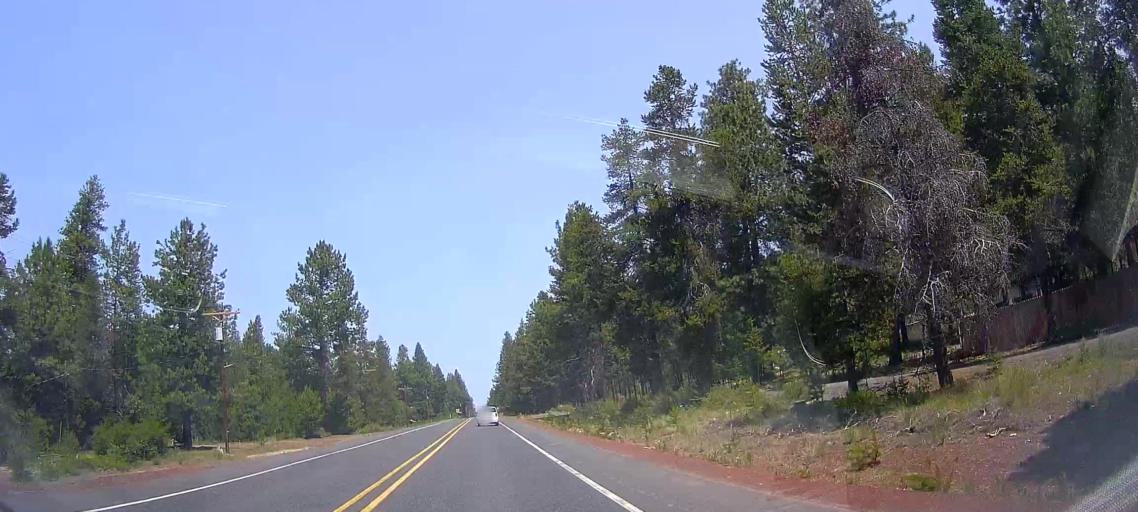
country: US
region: Oregon
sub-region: Deschutes County
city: La Pine
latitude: 43.4693
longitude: -121.6909
